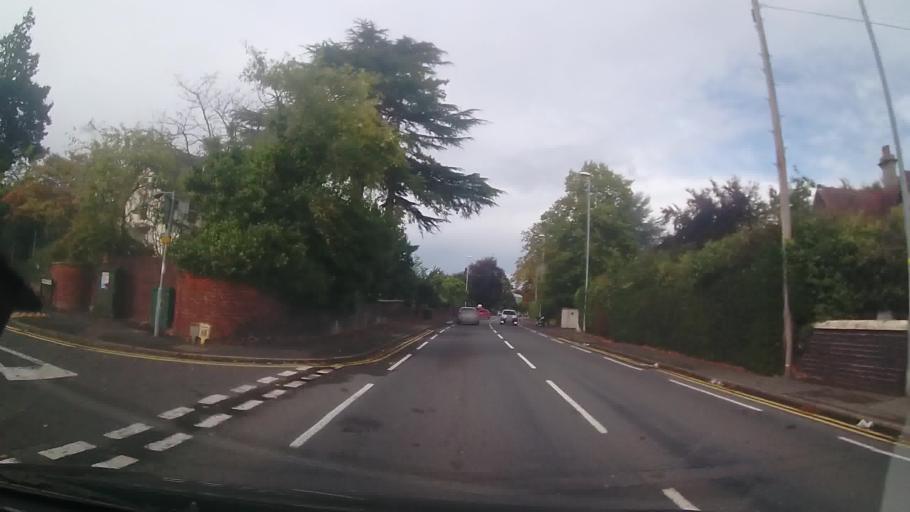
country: GB
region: England
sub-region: Worcestershire
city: Kidderminster
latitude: 52.3921
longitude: -2.2616
